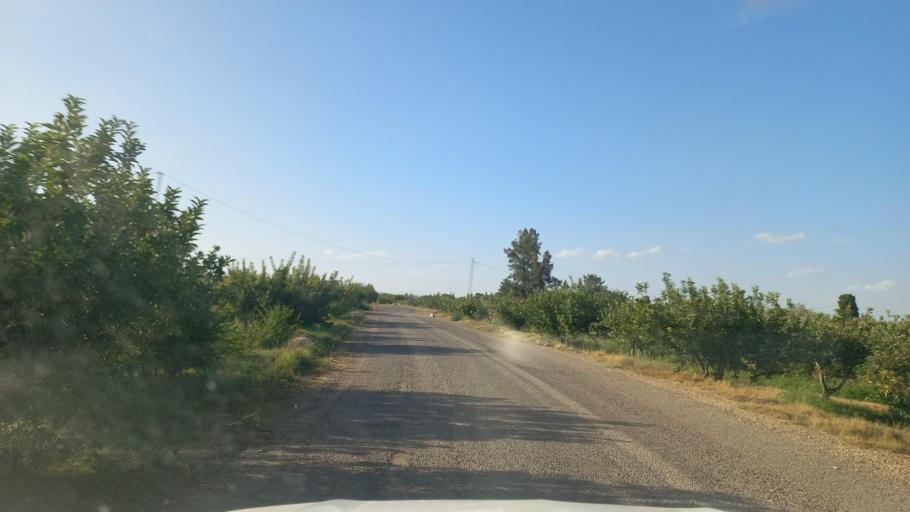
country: TN
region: Al Qasrayn
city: Kasserine
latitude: 35.2649
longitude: 9.0282
